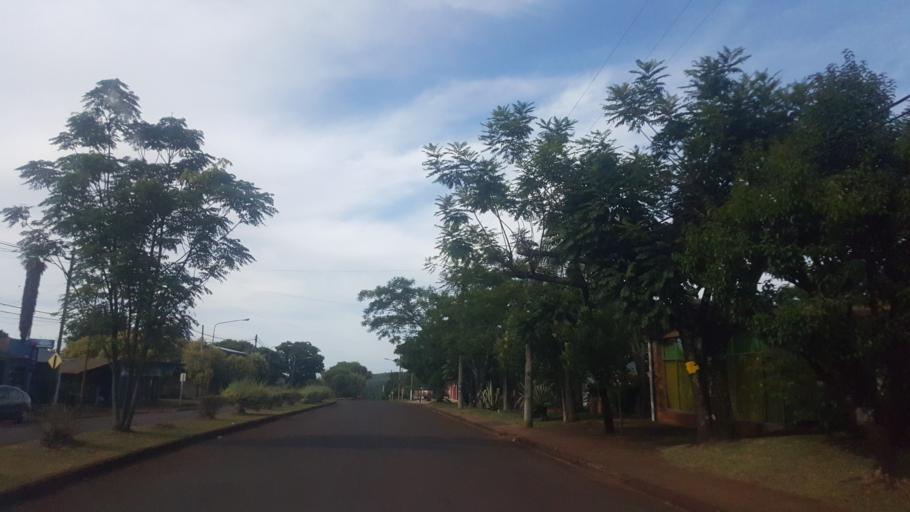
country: AR
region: Misiones
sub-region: Departamento de Leandro N. Alem
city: Leandro N. Alem
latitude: -27.5954
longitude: -55.3236
